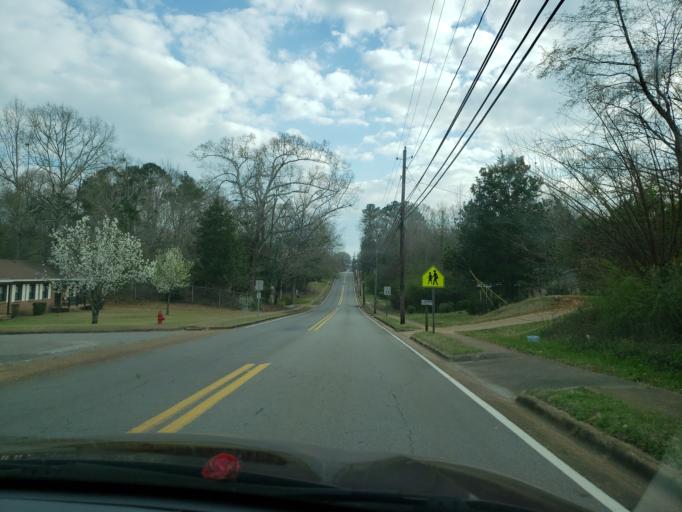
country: US
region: Alabama
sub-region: Hale County
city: Greensboro
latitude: 32.7095
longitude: -87.5921
